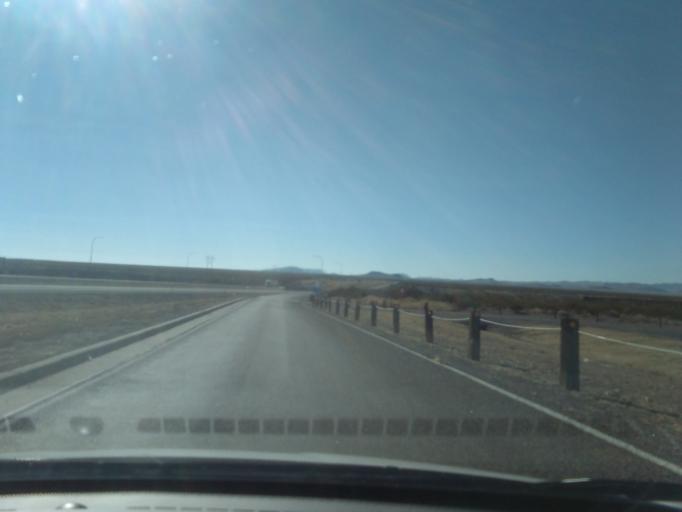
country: US
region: New Mexico
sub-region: Sierra County
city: Elephant Butte
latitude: 33.6218
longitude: -107.1392
